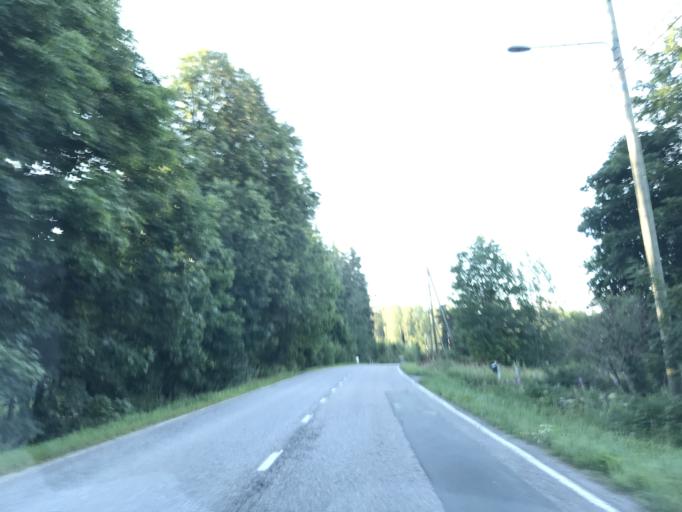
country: FI
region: Uusimaa
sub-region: Helsinki
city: Nurmijaervi
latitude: 60.3773
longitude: 24.6763
